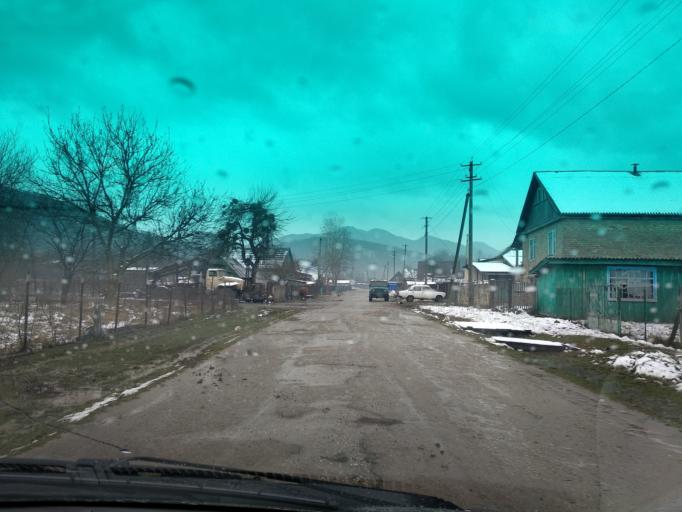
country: RU
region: Krasnodarskiy
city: Khadyzhensk
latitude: 44.2107
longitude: 39.4274
